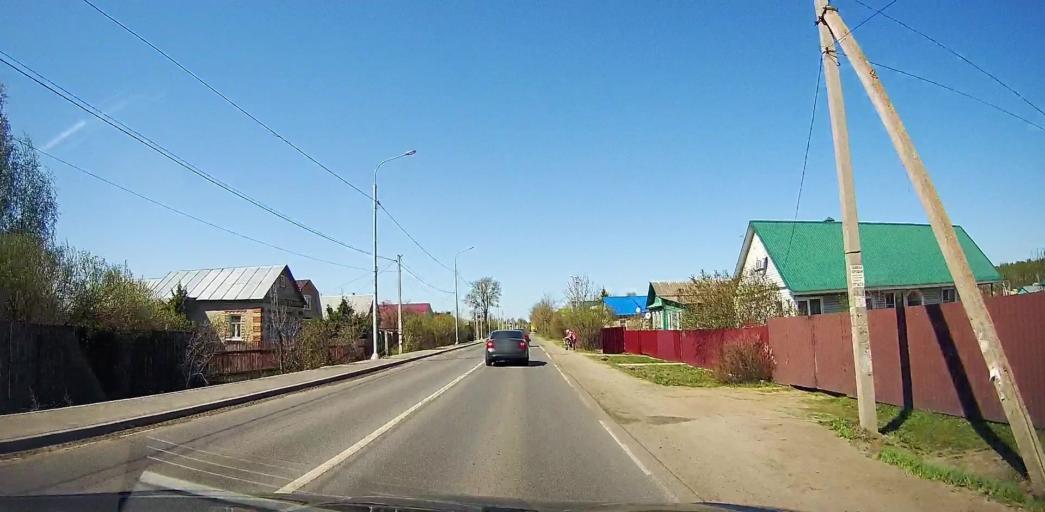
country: RU
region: Moskovskaya
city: Beloozerskiy
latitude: 55.4752
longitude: 38.4095
